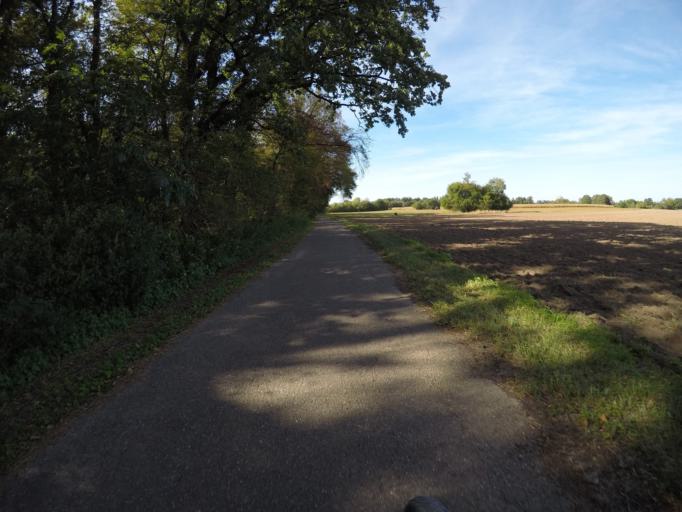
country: DE
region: Baden-Wuerttemberg
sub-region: Karlsruhe Region
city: Kronau
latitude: 49.2330
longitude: 8.6202
